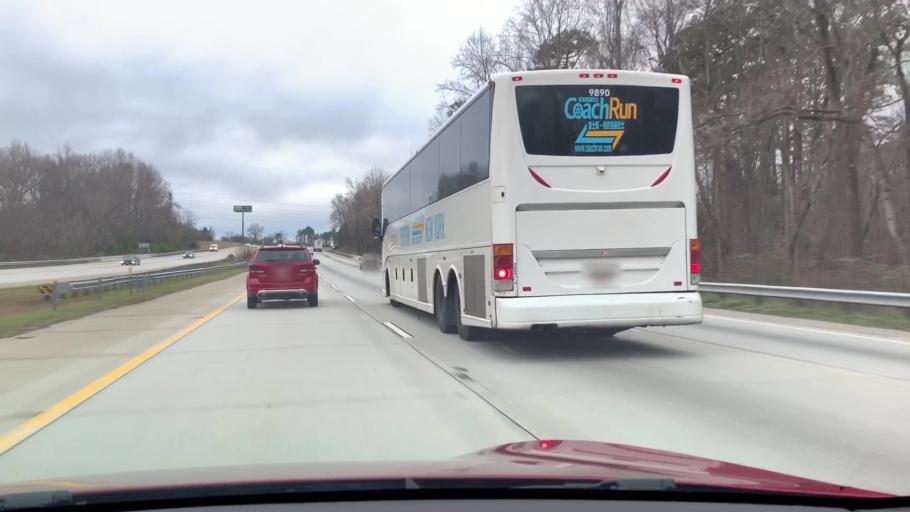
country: US
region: South Carolina
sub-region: Florence County
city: Florence
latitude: 34.2487
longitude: -79.7657
